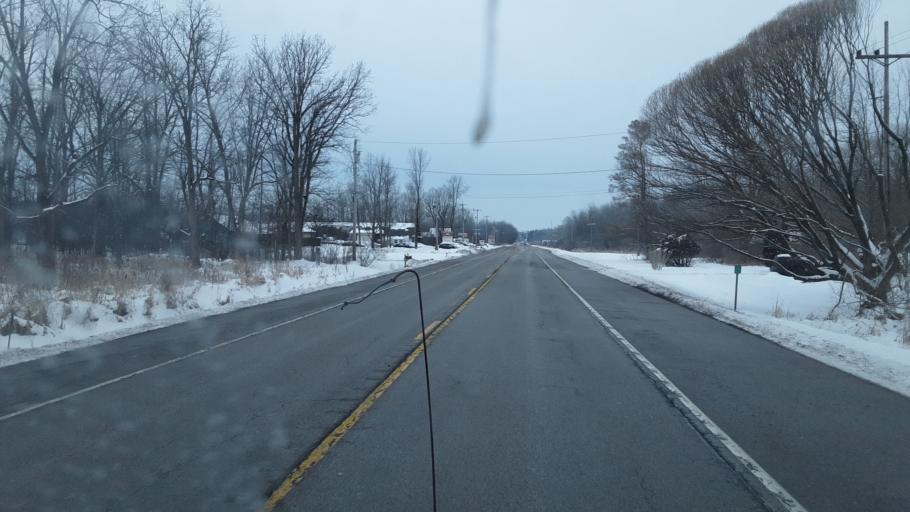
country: US
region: New York
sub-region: Wayne County
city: Newark
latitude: 43.0553
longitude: -77.0555
